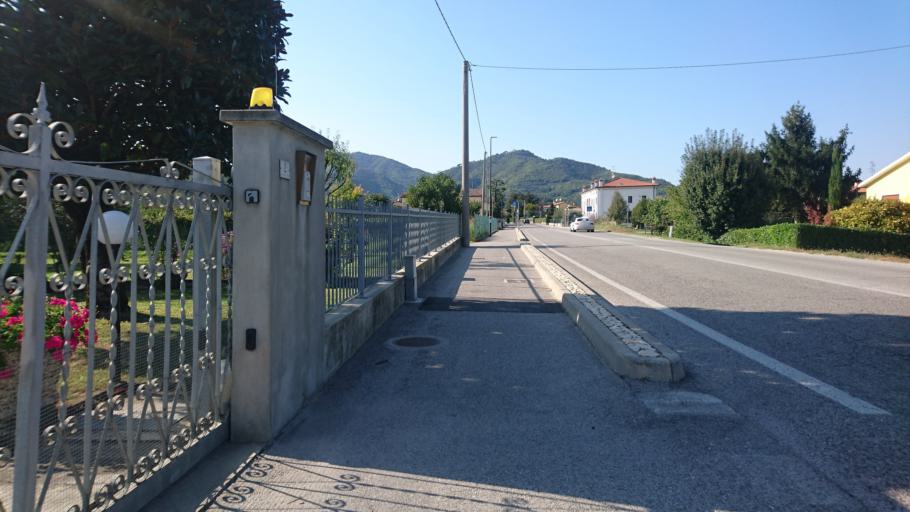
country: IT
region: Veneto
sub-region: Provincia di Padova
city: Galzignano
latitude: 45.3042
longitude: 11.7446
